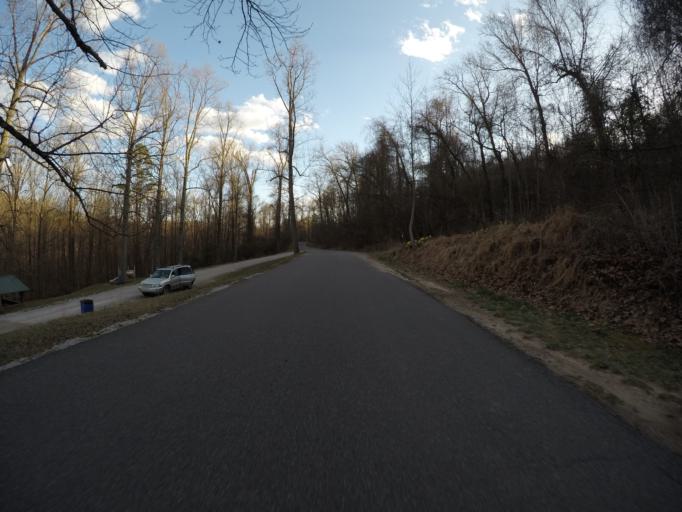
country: US
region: West Virginia
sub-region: Kanawha County
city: Charleston
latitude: 38.3922
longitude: -81.5720
